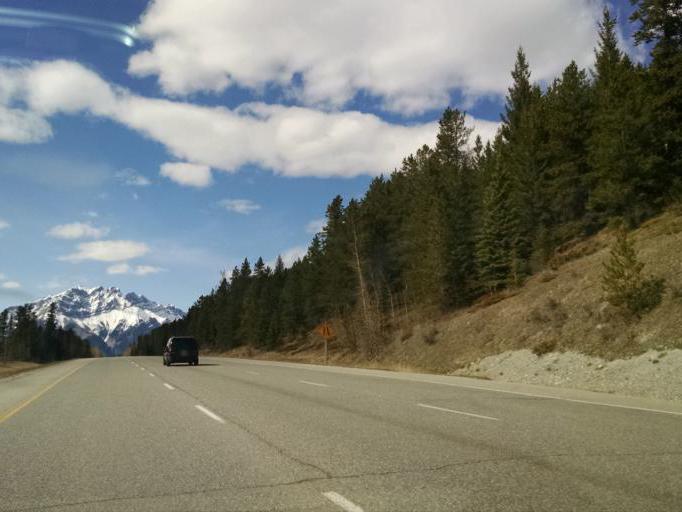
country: CA
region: Alberta
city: Canmore
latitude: 51.1402
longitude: -115.4135
